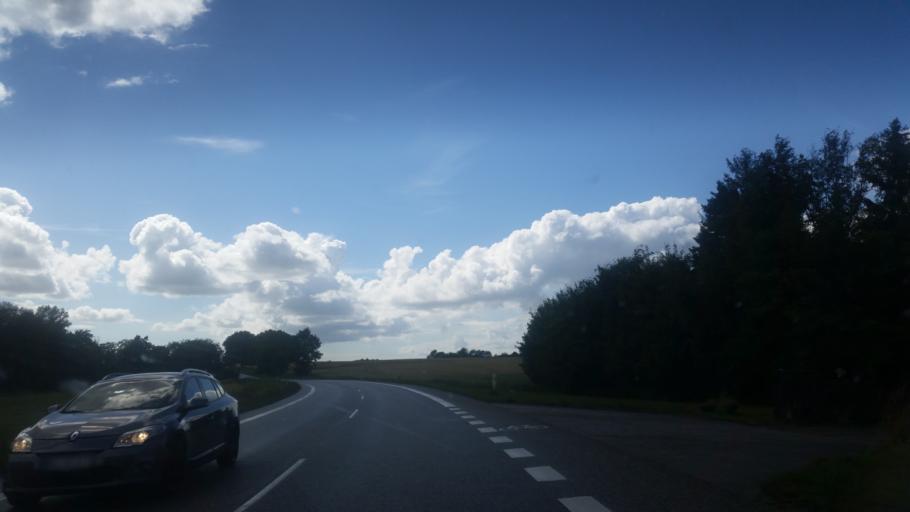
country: DK
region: Zealand
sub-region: Holbaek Kommune
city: Svinninge
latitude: 55.7276
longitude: 11.5765
